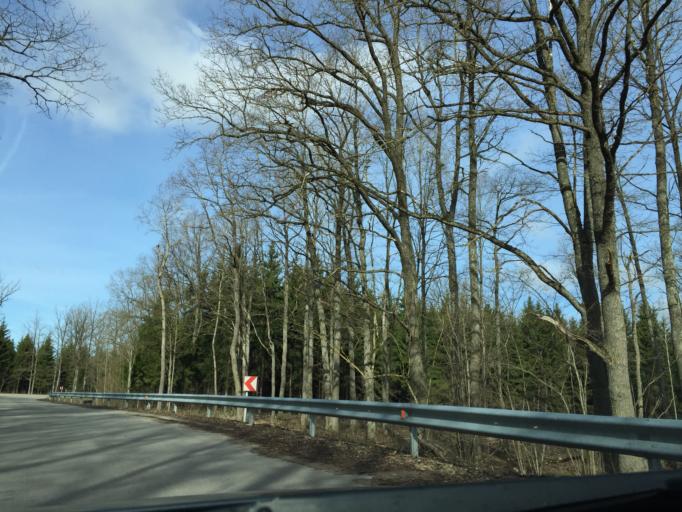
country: LT
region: Siauliu apskritis
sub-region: Joniskis
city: Joniskis
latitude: 56.1768
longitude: 23.5470
